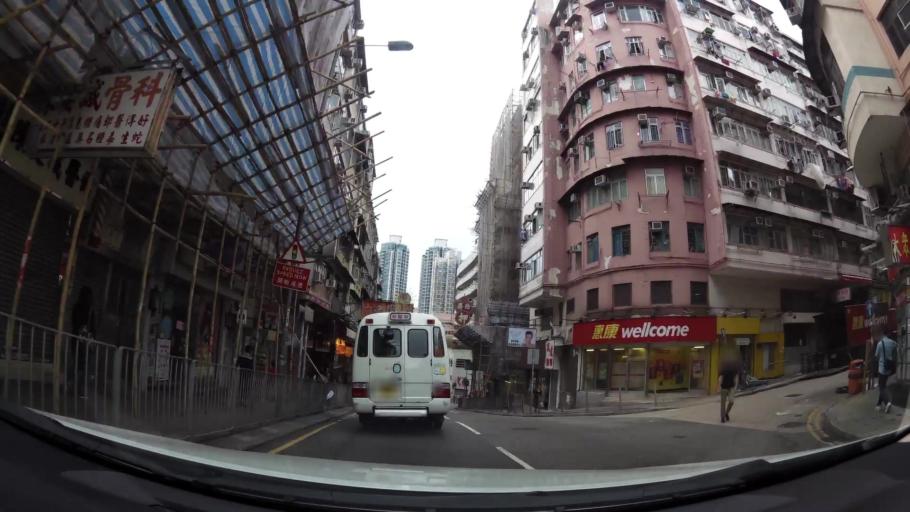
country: HK
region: Wong Tai Sin
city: Wong Tai Sin
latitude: 22.3447
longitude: 114.1975
